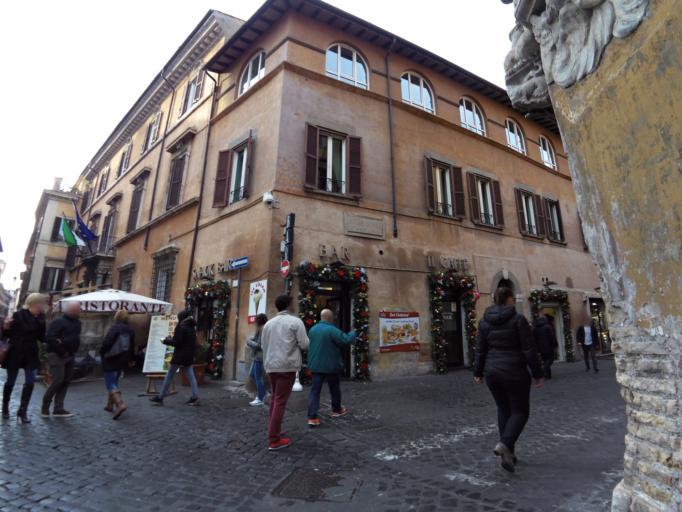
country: IT
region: Latium
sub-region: Citta metropolitana di Roma Capitale
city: Rome
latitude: 41.9000
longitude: 12.4839
